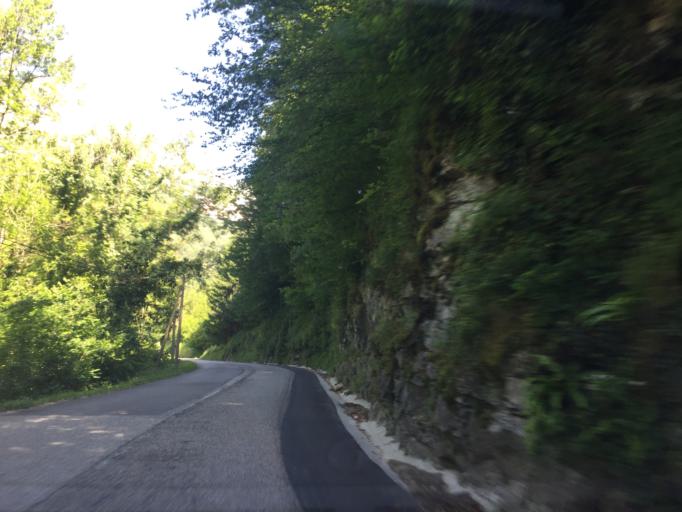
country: FR
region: Rhone-Alpes
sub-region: Departement de l'Isere
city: Pont-en-Royans
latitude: 45.0437
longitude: 5.3680
